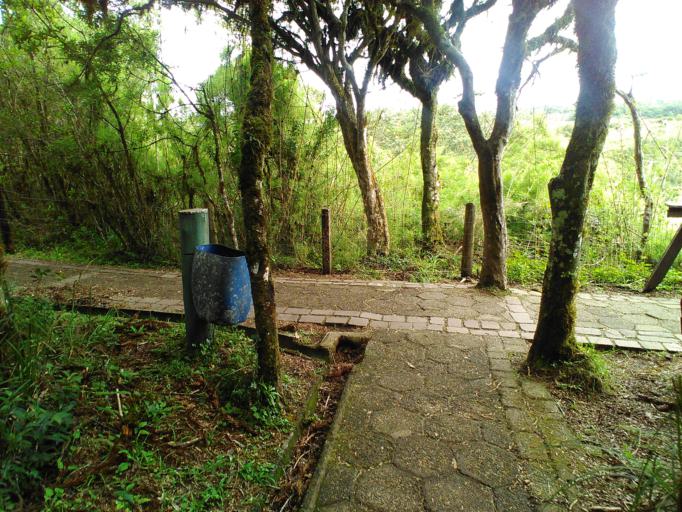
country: BR
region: Rio Grande do Sul
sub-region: Torres
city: Torres
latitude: -29.1593
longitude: -50.0791
